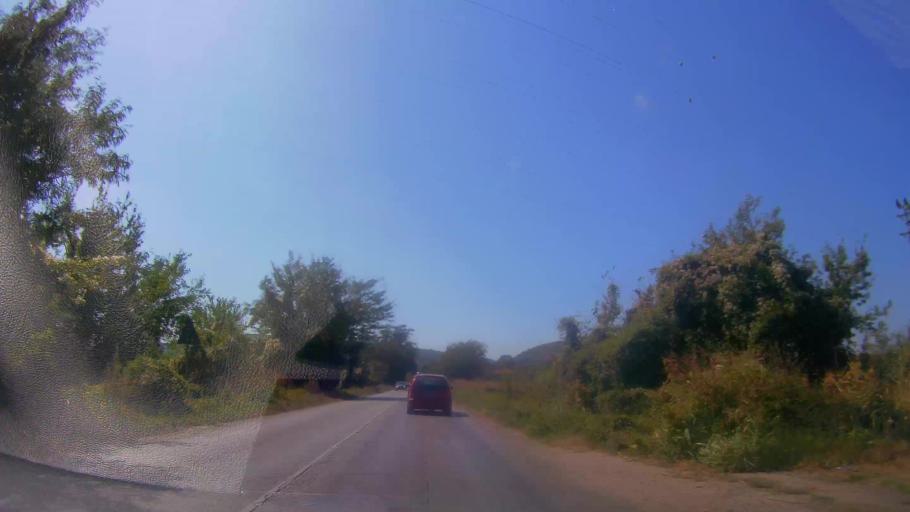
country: BG
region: Veliko Turnovo
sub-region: Obshtina Gorna Oryakhovitsa
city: Purvomaytsi
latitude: 43.1496
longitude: 25.6161
